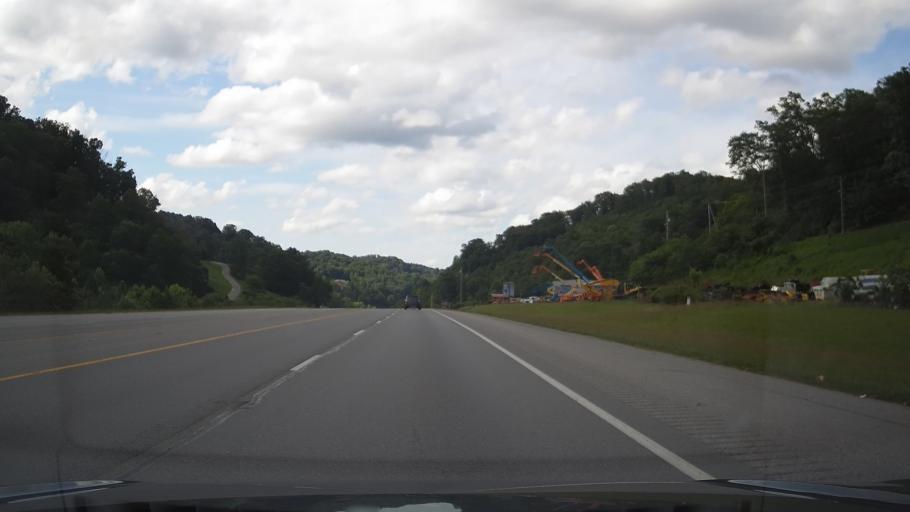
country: US
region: Kentucky
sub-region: Floyd County
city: Prestonsburg
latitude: 37.6985
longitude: -82.7922
